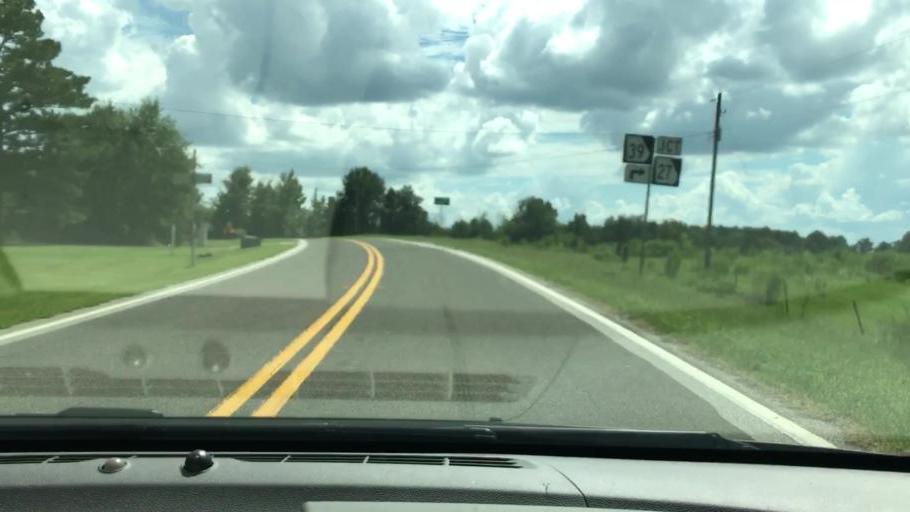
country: US
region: Georgia
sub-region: Quitman County
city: Georgetown
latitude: 31.8931
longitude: -85.0827
